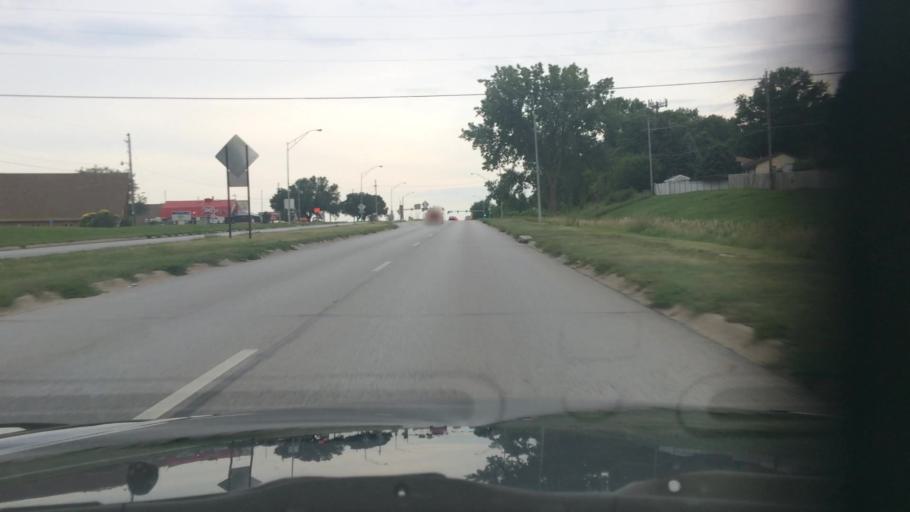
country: US
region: Nebraska
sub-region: Douglas County
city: Ralston
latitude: 41.1938
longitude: -96.0431
